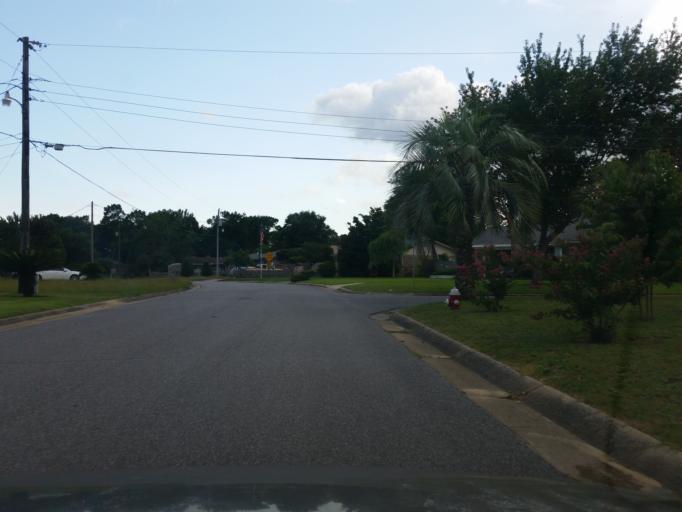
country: US
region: Florida
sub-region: Escambia County
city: Ferry Pass
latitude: 30.5114
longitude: -87.1780
